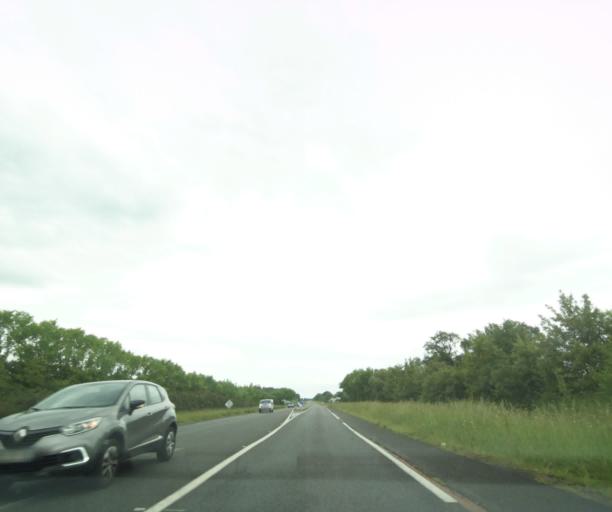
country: FR
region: Poitou-Charentes
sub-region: Departement des Deux-Sevres
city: Airvault
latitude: 46.7965
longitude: -0.2133
